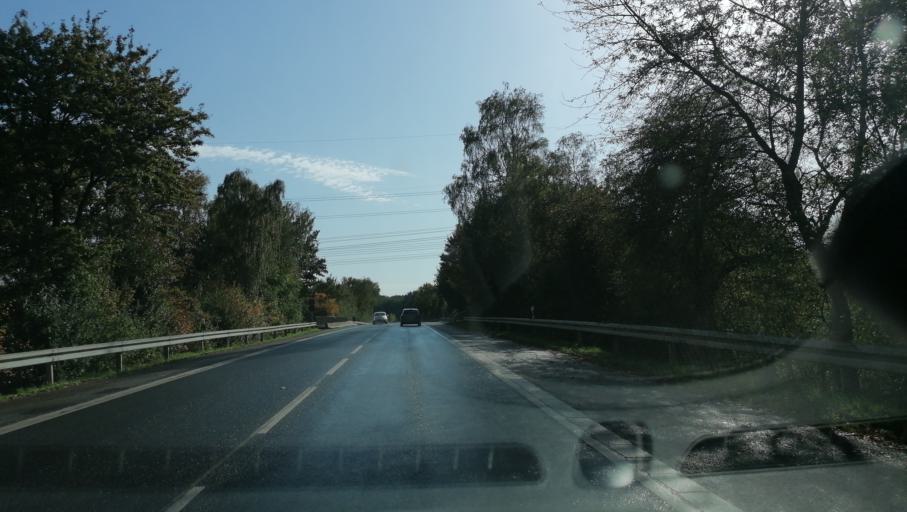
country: DE
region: North Rhine-Westphalia
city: Datteln
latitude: 51.6319
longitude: 7.3492
